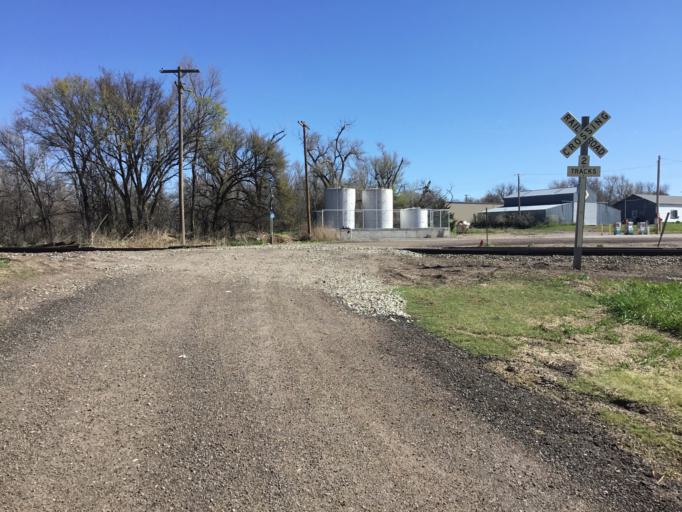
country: US
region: Kansas
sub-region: Phillips County
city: Phillipsburg
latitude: 39.8310
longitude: -99.5755
